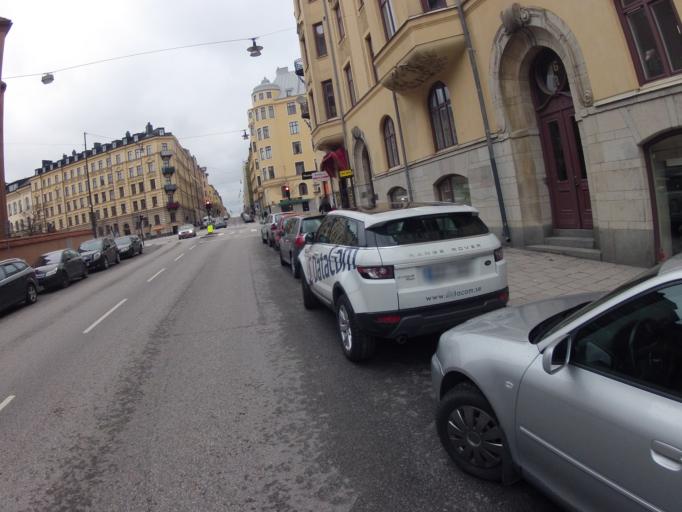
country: SE
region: Stockholm
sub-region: Stockholms Kommun
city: Stockholm
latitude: 59.3423
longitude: 18.0450
